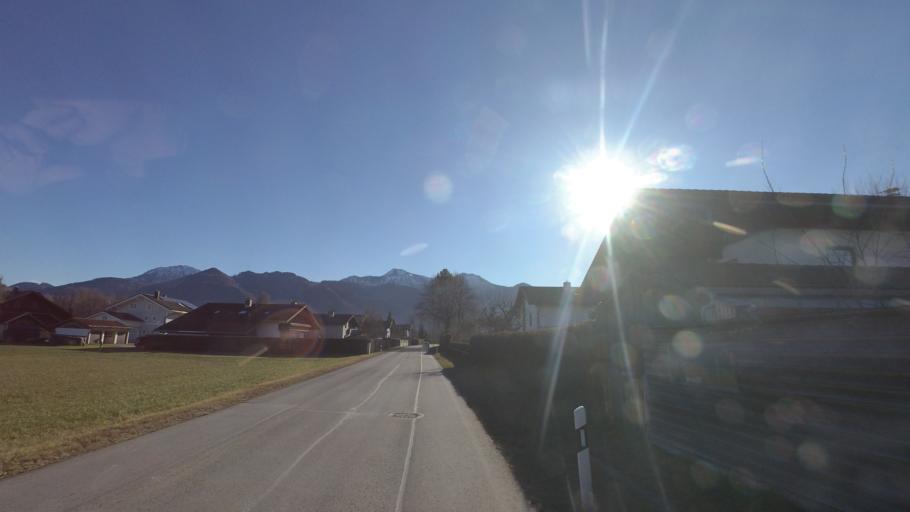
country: DE
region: Bavaria
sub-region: Upper Bavaria
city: Ubersee
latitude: 47.8094
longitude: 12.4811
